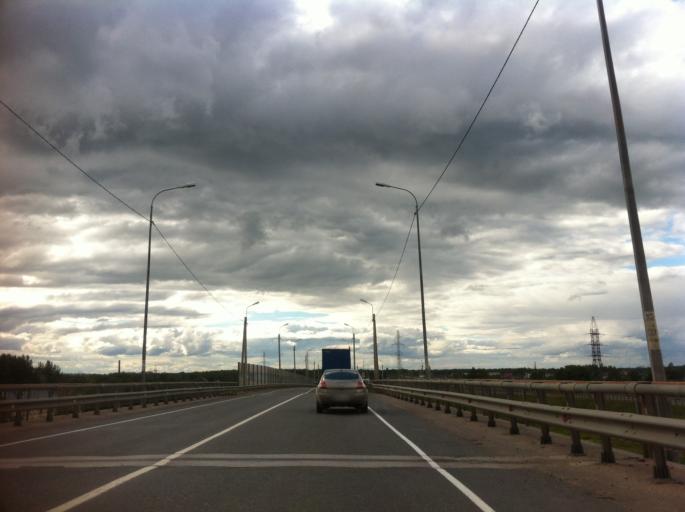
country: RU
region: Pskov
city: Pskov
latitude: 57.8334
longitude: 28.4217
